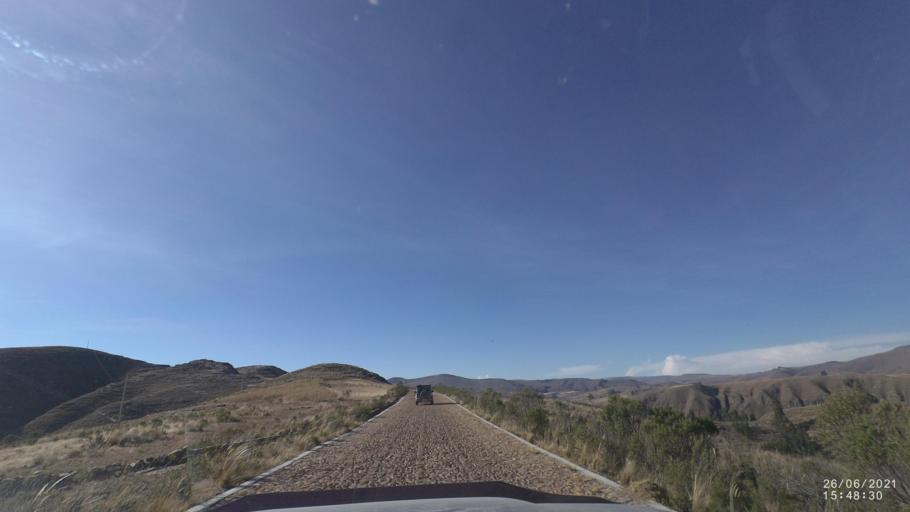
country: BO
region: Cochabamba
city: Arani
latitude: -17.8624
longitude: -65.6959
